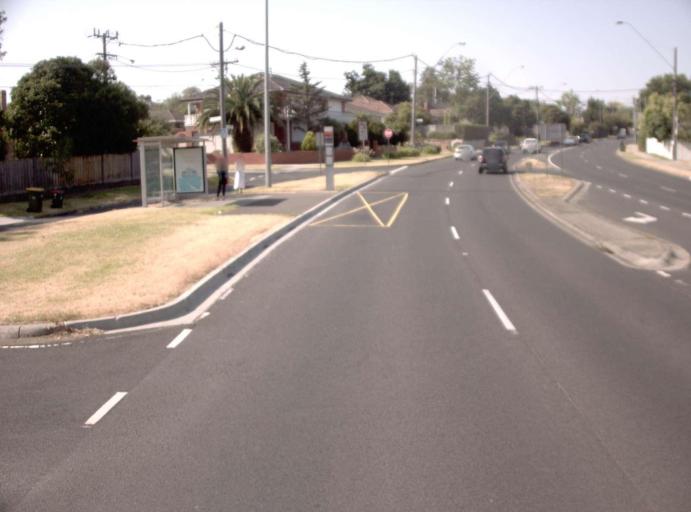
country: AU
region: Victoria
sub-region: Whitehorse
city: Box Hill North
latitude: -37.7985
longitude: 145.1272
